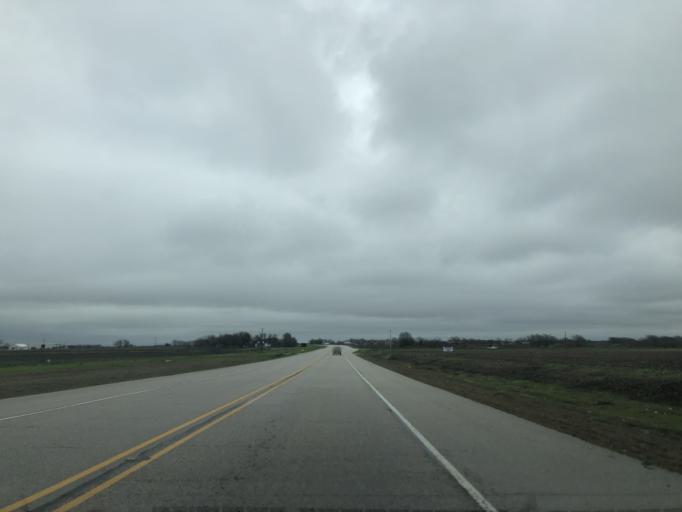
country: US
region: Texas
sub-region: Williamson County
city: Hutto
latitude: 30.6016
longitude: -97.5093
